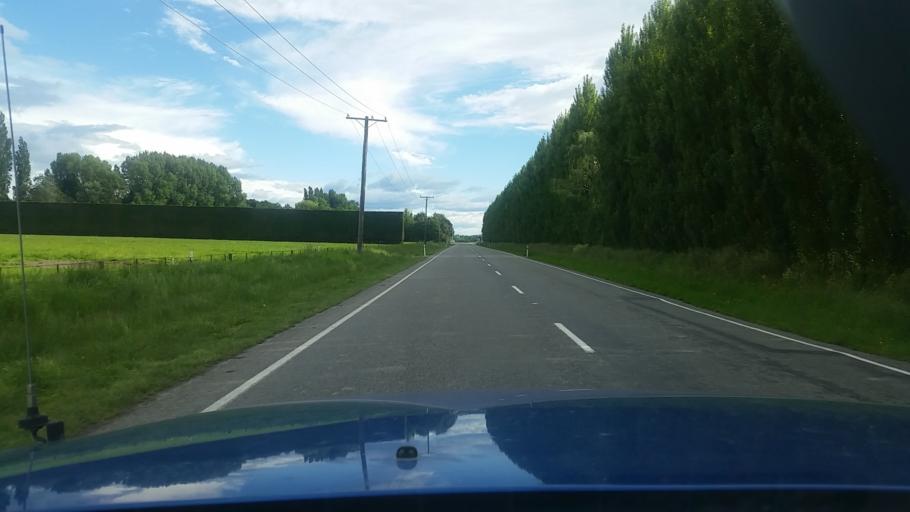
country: NZ
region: Canterbury
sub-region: Ashburton District
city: Ashburton
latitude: -43.8606
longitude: 171.7303
